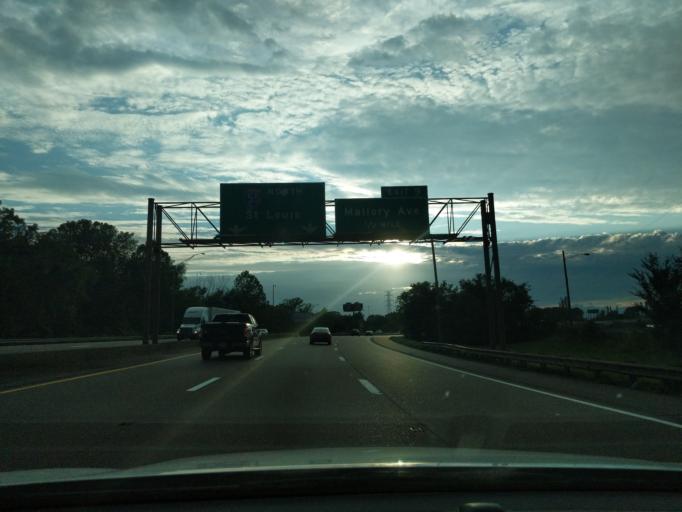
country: US
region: Tennessee
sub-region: Shelby County
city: New South Memphis
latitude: 35.0796
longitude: -90.0672
